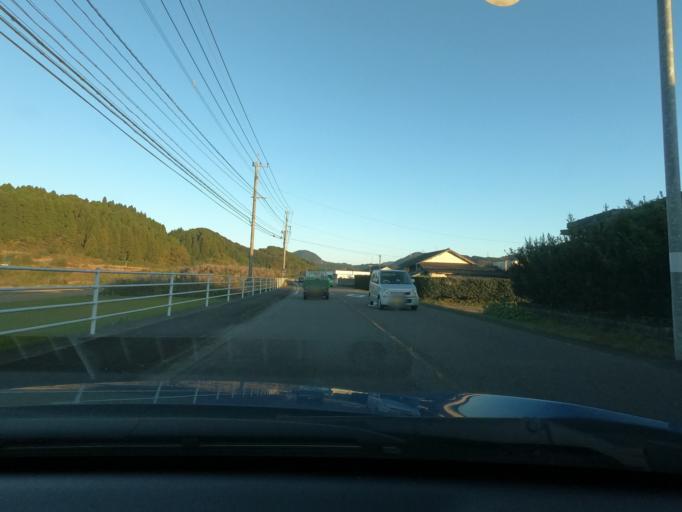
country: JP
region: Kagoshima
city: Satsumasendai
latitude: 31.7942
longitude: 130.4474
